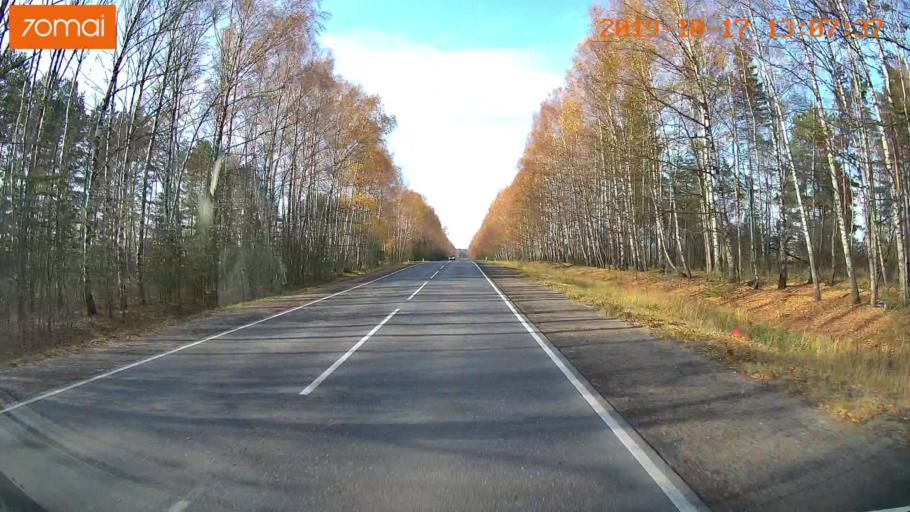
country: RU
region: Rjazan
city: Syntul
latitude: 54.9834
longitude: 41.2865
